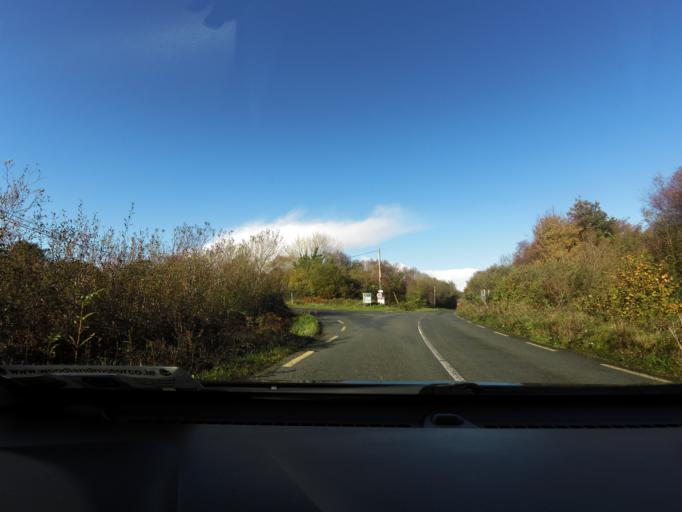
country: IE
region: Connaught
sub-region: Maigh Eo
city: Ballinrobe
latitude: 53.7000
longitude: -9.2926
